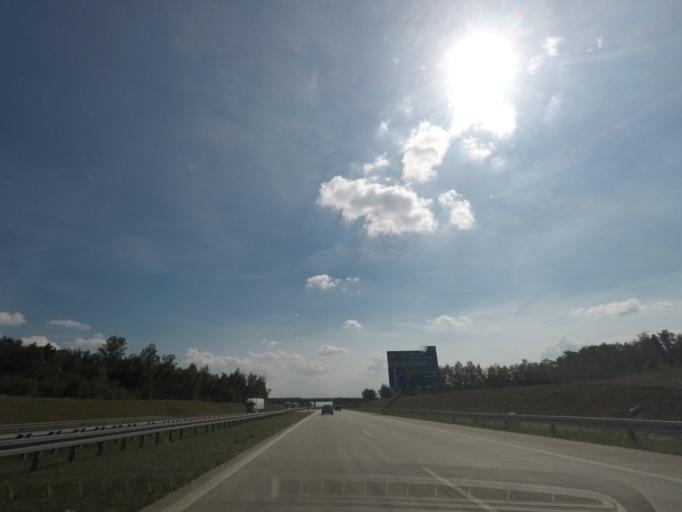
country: PL
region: Lodz Voivodeship
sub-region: Powiat lodzki wschodni
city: Brojce
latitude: 51.6638
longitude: 19.5838
